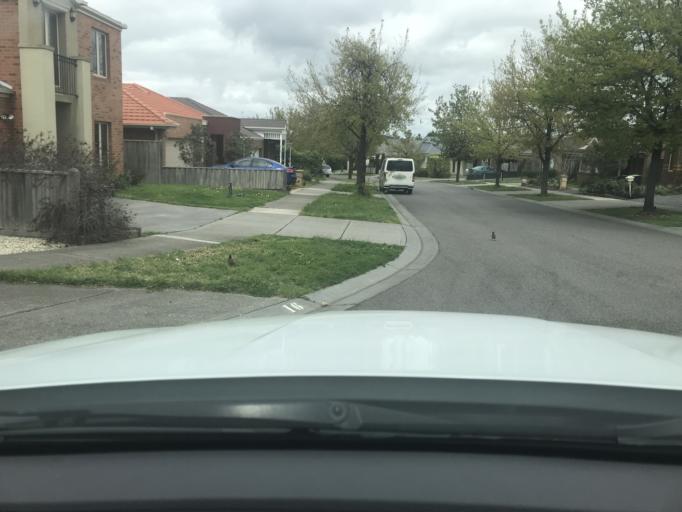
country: AU
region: Victoria
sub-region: Hume
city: Craigieburn
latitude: -37.5744
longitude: 144.9274
